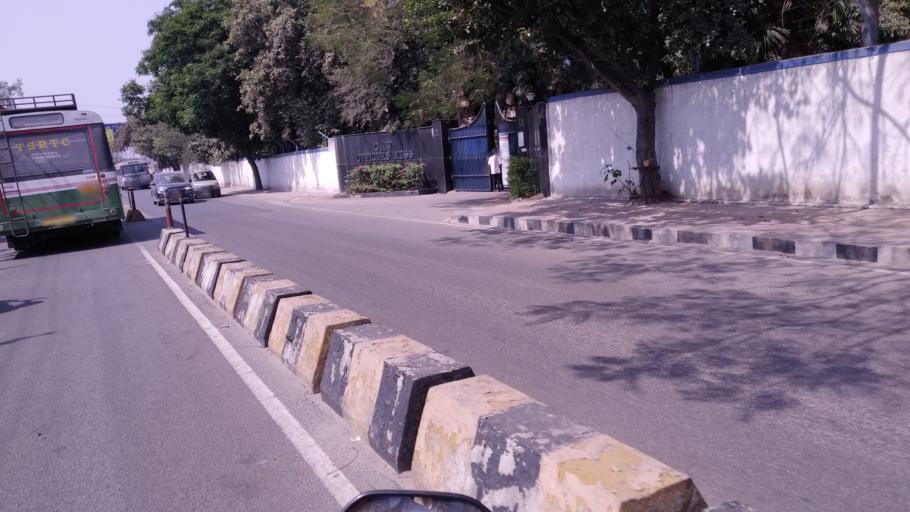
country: IN
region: Telangana
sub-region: Hyderabad
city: Malkajgiri
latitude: 17.4503
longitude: 78.4893
